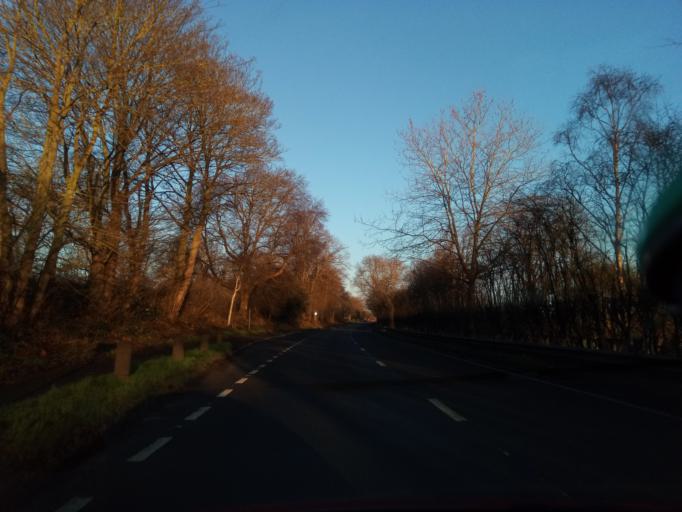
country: GB
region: England
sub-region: Nottinghamshire
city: Sutton Bonington
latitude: 52.8142
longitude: -1.2661
